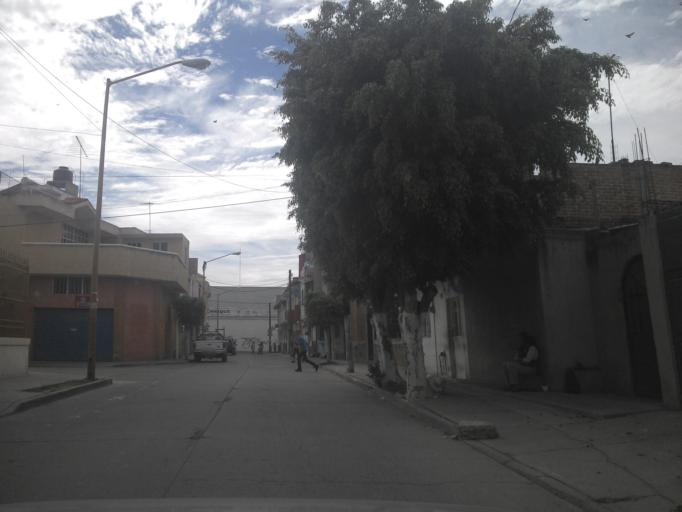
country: MX
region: Guanajuato
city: San Francisco del Rincon
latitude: 21.0096
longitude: -101.8553
